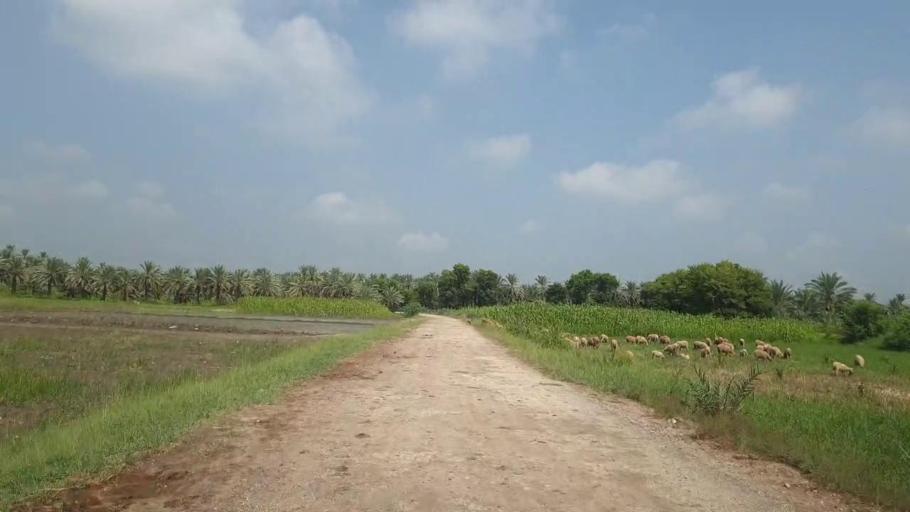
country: PK
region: Sindh
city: Pir jo Goth
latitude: 27.6058
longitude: 68.6921
